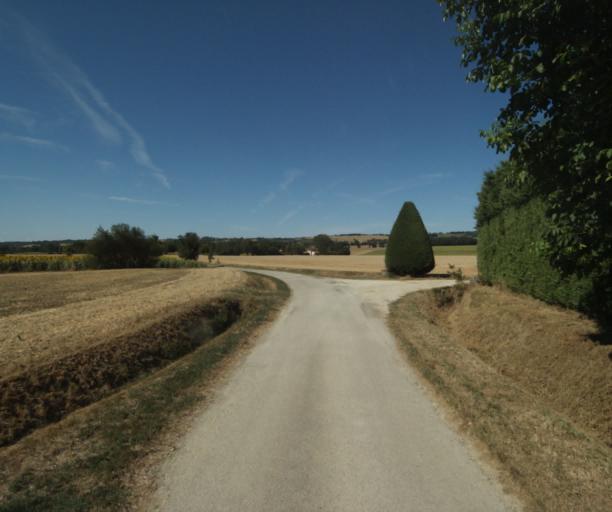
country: FR
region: Midi-Pyrenees
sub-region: Departement de la Haute-Garonne
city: Saint-Felix-Lauragais
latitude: 43.5023
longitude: 1.8951
